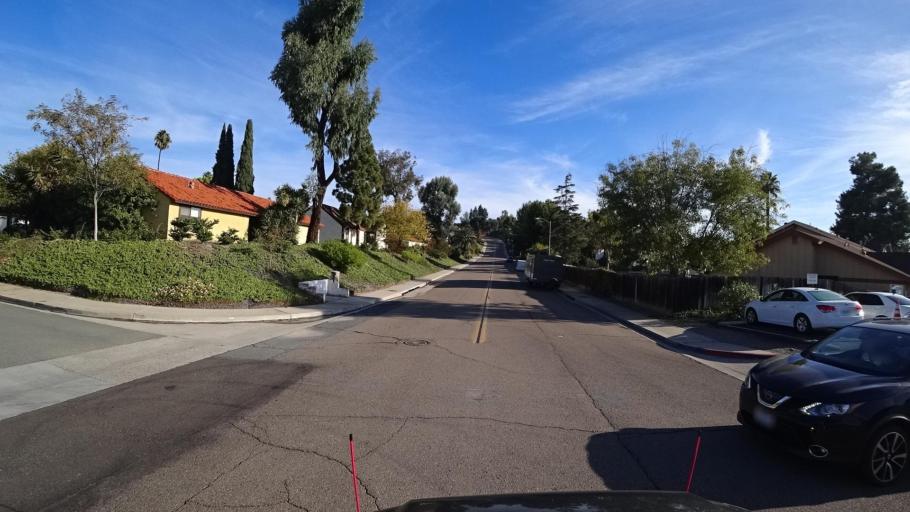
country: US
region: California
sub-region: San Diego County
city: Spring Valley
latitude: 32.7342
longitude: -116.9808
